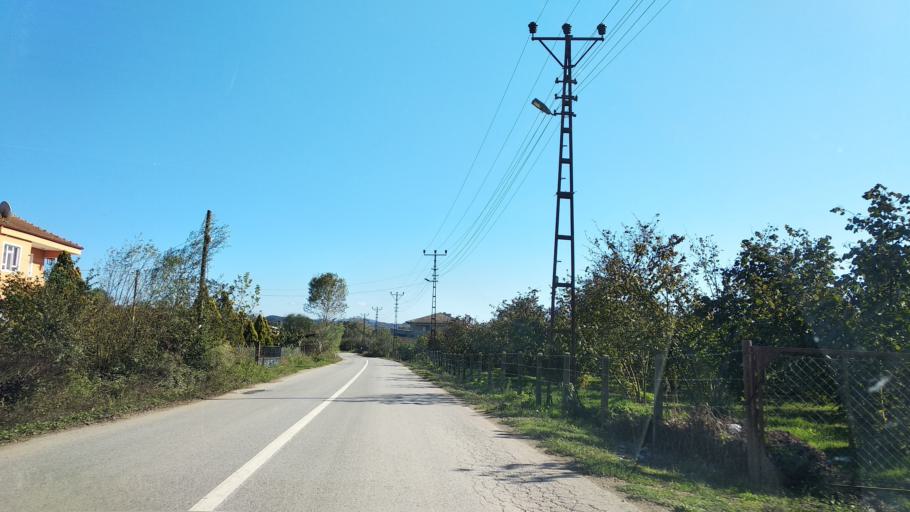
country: TR
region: Sakarya
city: Ortakoy
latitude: 41.0261
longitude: 30.5977
